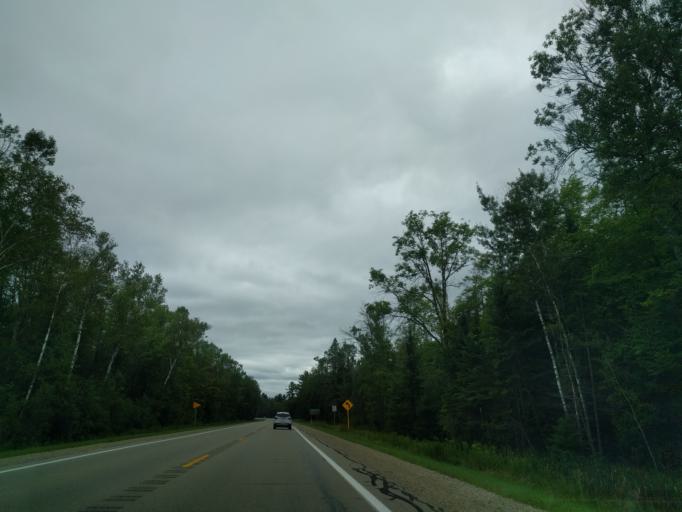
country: US
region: Michigan
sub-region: Delta County
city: Escanaba
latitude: 45.4352
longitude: -87.3482
